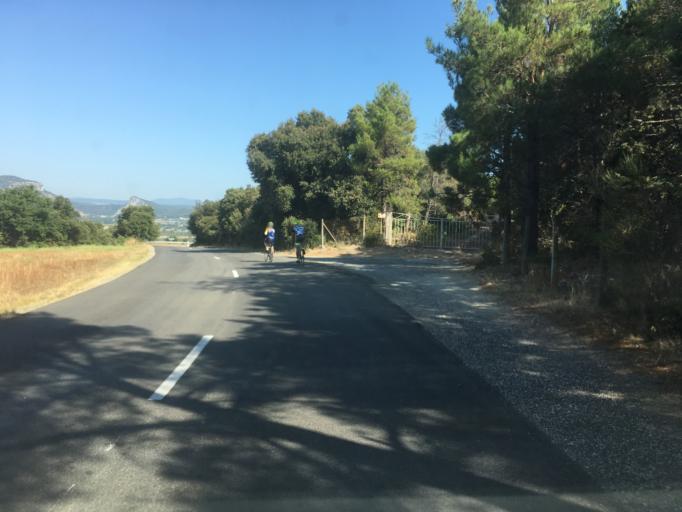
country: FR
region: Provence-Alpes-Cote d'Azur
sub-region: Departement des Alpes-de-Haute-Provence
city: Volx
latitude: 43.8460
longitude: 5.8772
